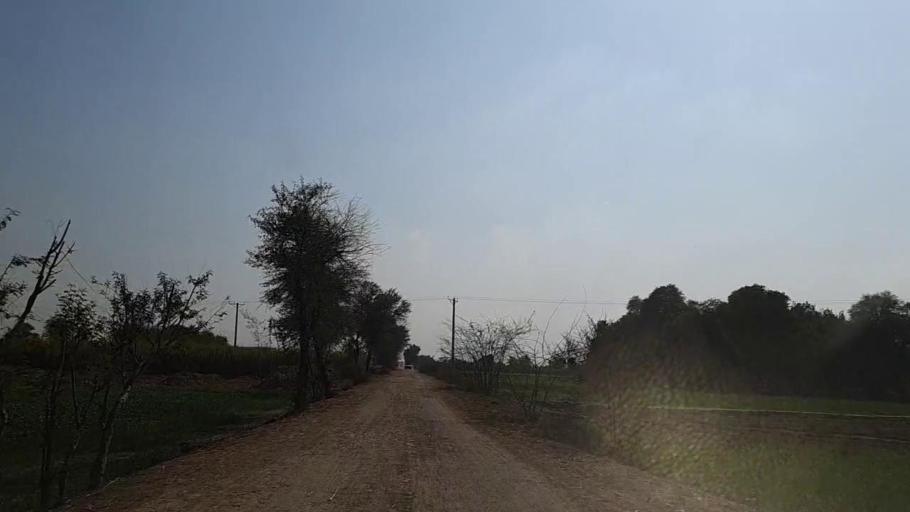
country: PK
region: Sindh
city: Daur
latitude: 26.4249
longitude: 68.2368
